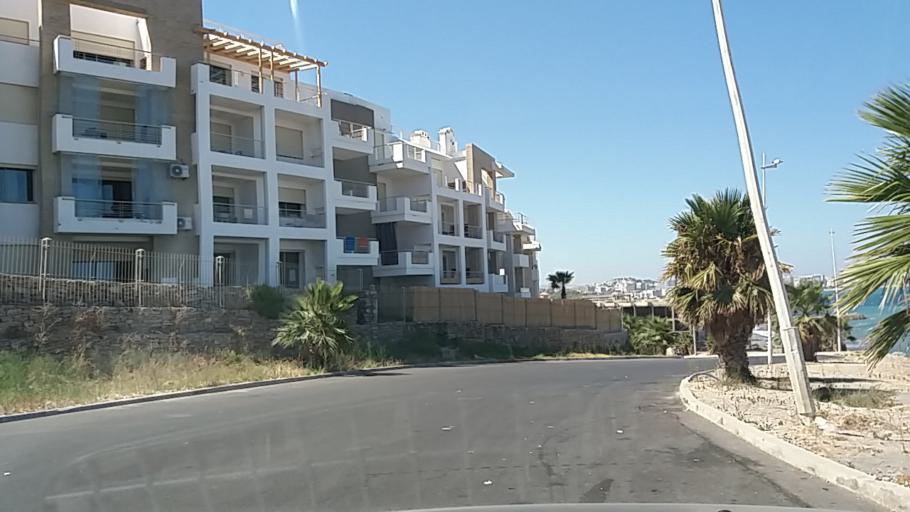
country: MA
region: Tanger-Tetouan
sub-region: Tanger-Assilah
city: Tangier
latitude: 35.7917
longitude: -5.7558
